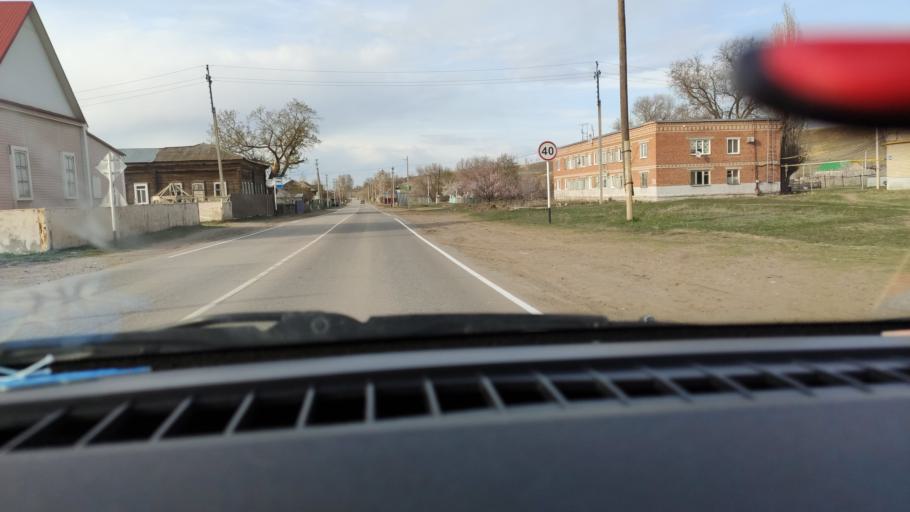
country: RU
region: Saratov
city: Privolzhskiy
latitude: 51.2090
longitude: 45.9188
